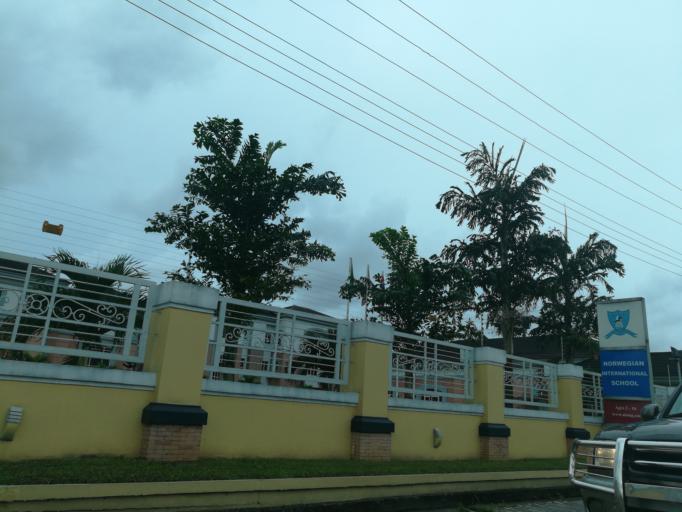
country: NG
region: Rivers
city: Port Harcourt
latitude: 4.8199
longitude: 6.9910
